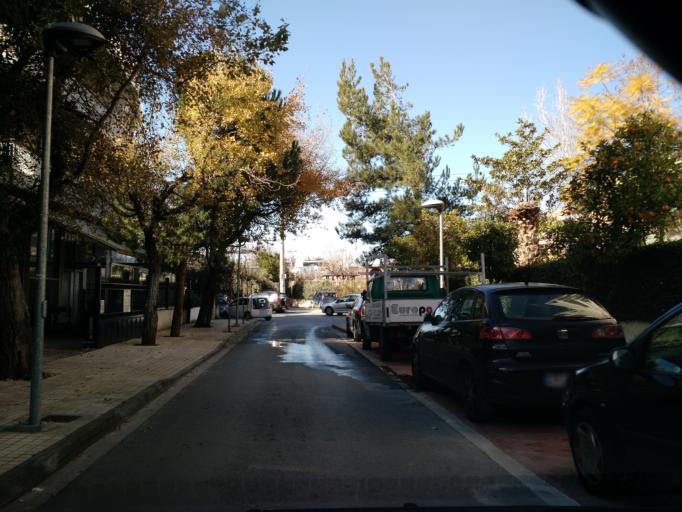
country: GR
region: Attica
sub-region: Nomarchia Athinas
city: Agia Paraskevi
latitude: 38.0204
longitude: 23.8216
